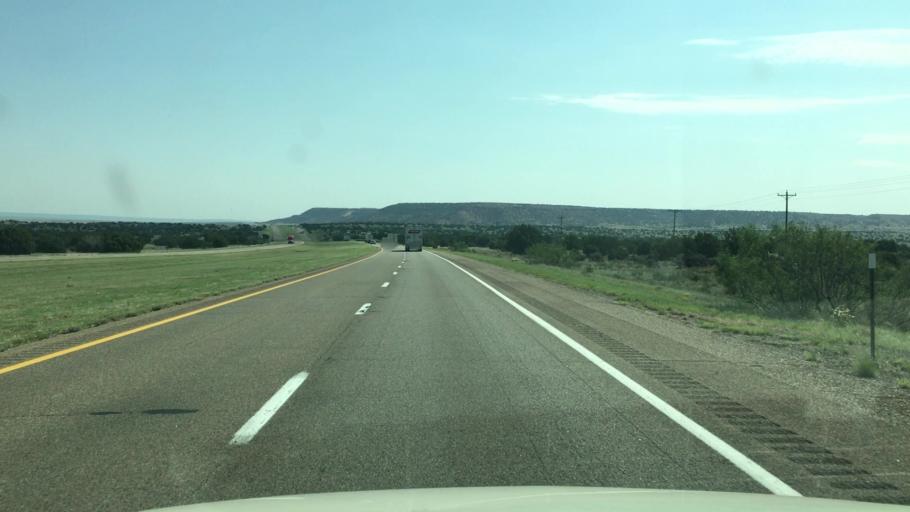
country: US
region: New Mexico
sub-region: Guadalupe County
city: Santa Rosa
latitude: 35.0152
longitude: -104.4466
